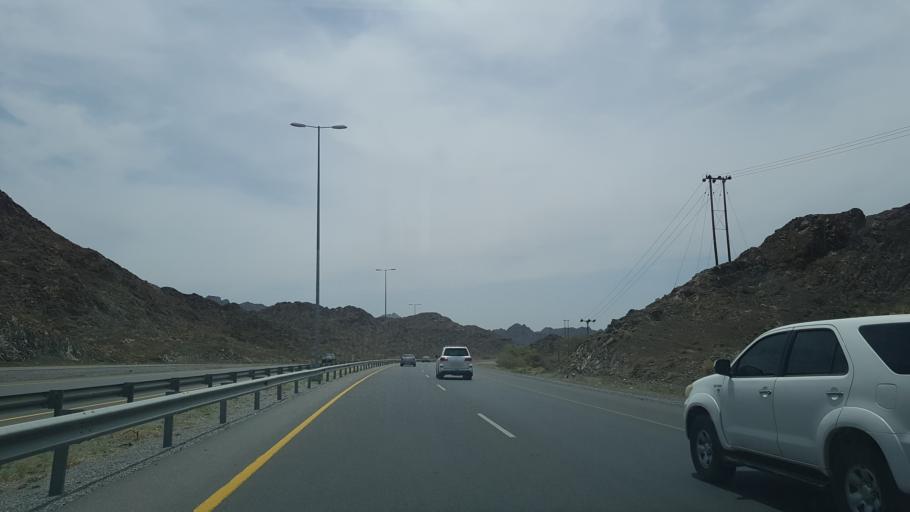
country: OM
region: Muhafazat ad Dakhiliyah
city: Izki
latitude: 22.9497
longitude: 57.7891
